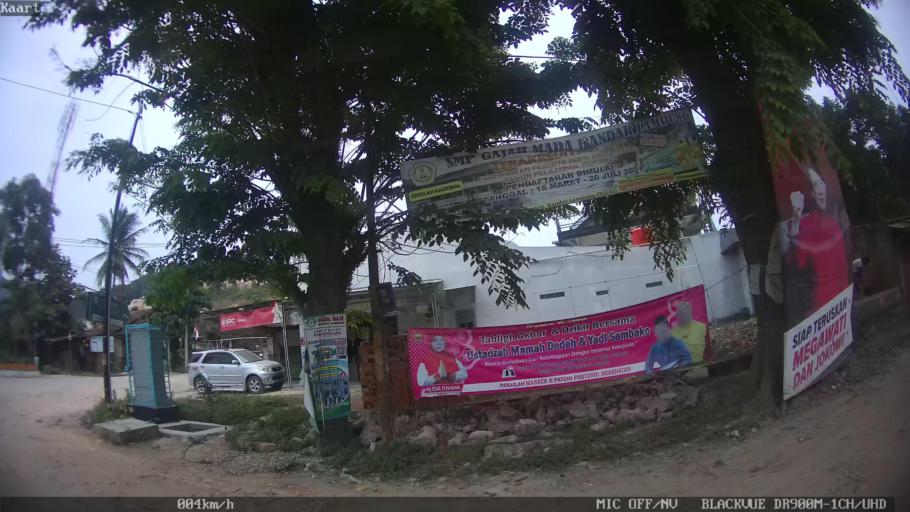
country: ID
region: Lampung
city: Bandarlampung
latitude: -5.4071
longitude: 105.3185
